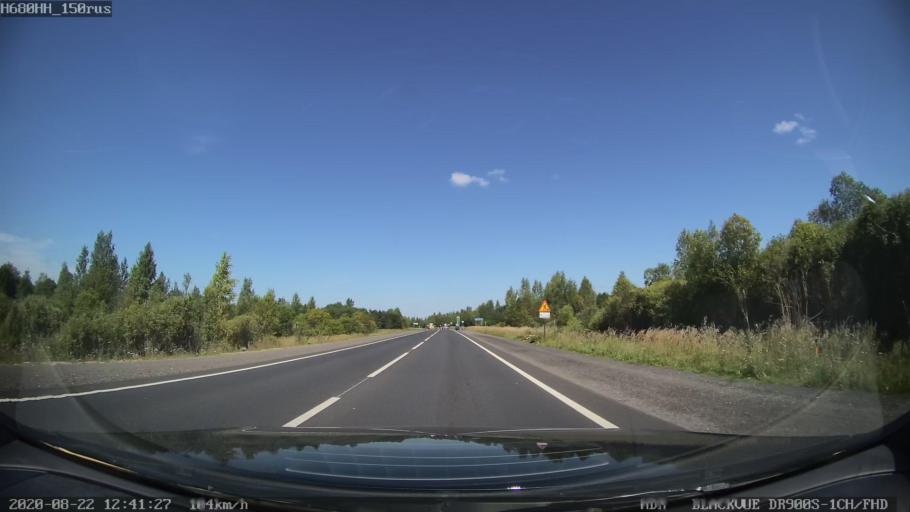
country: RU
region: Tverskaya
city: Rameshki
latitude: 57.3482
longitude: 36.0987
